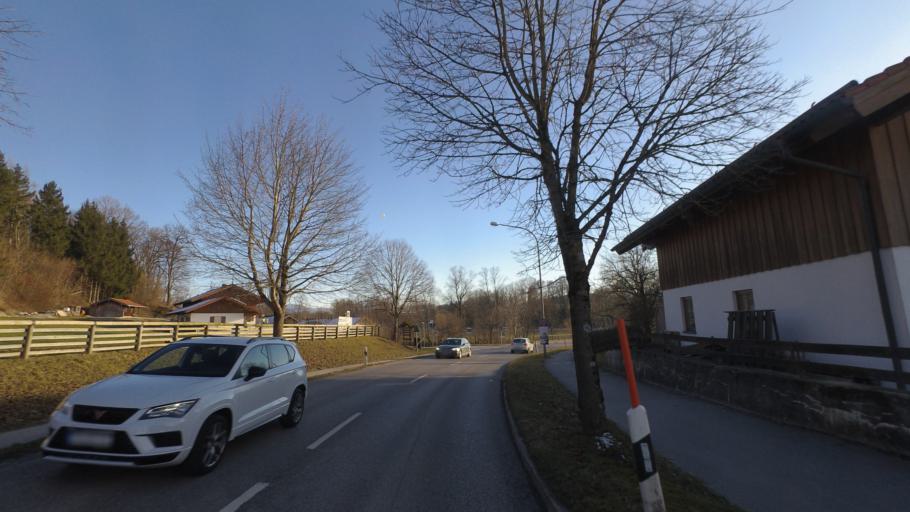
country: DE
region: Bavaria
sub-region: Upper Bavaria
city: Traunreut
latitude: 47.9390
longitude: 12.5993
